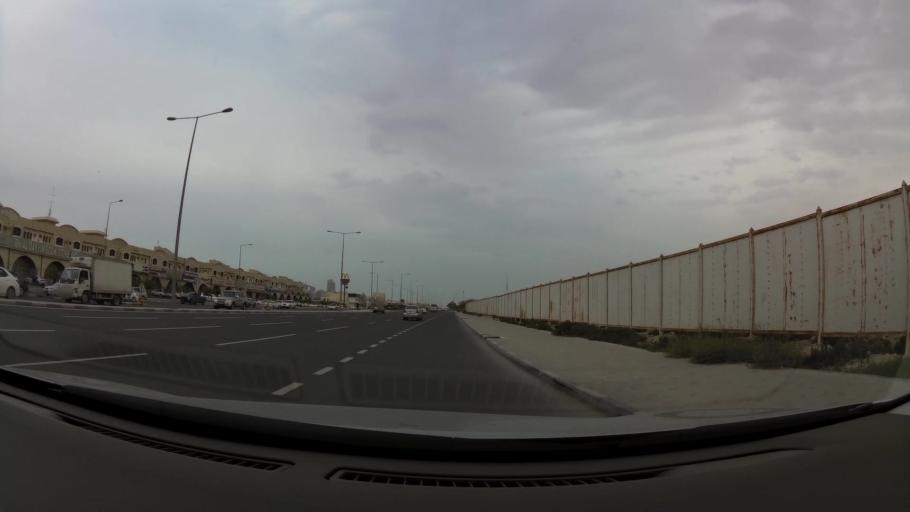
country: QA
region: Baladiyat ad Dawhah
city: Doha
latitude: 25.3216
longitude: 51.4875
